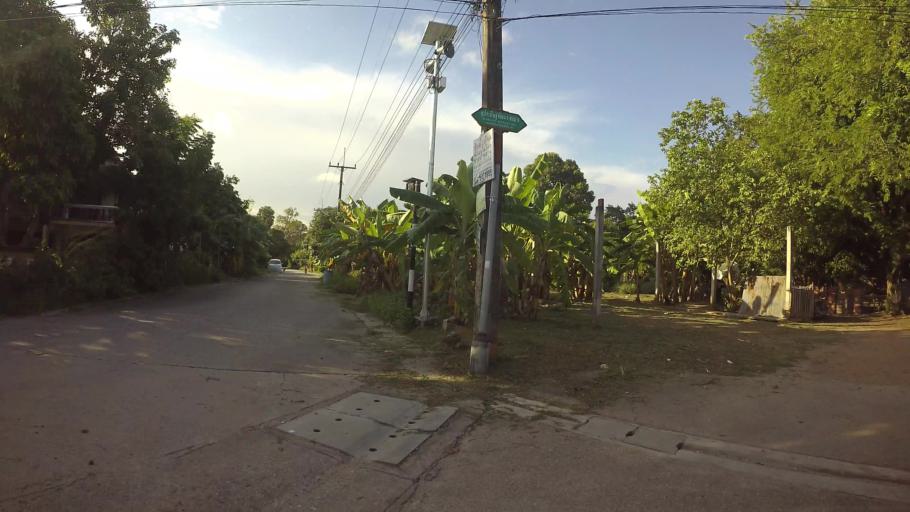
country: TH
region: Rayong
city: Rayong
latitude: 12.6848
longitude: 101.2900
